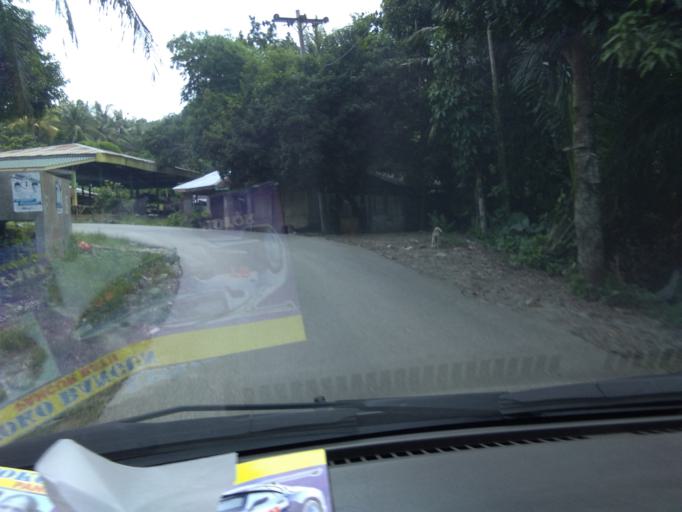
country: ID
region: North Sumatra
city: Deli Tua
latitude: 3.3052
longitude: 98.8084
